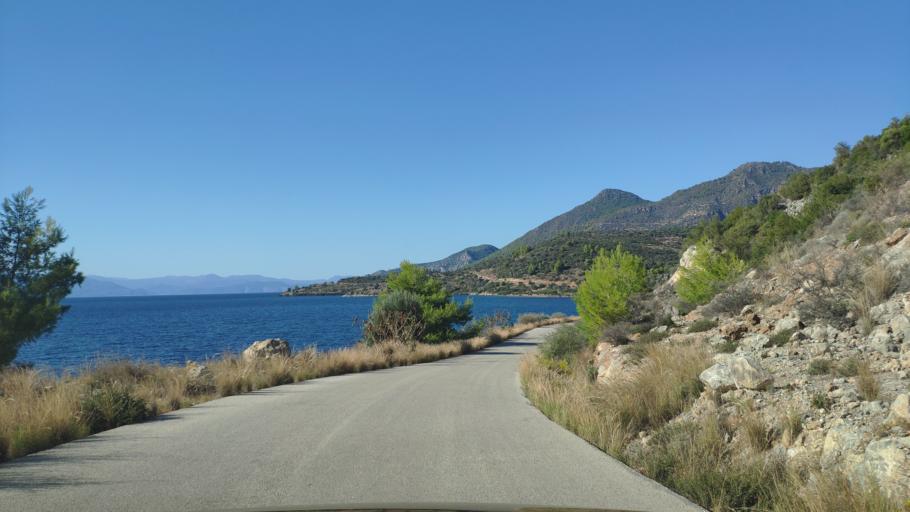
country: GR
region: Attica
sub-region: Nomos Piraios
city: Galatas
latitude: 37.5713
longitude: 23.3605
